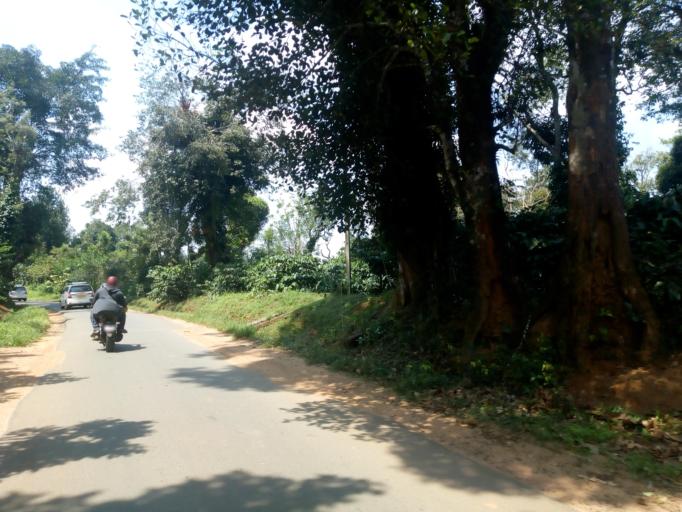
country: IN
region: Karnataka
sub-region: Kodagu
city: Ponnampet
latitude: 12.0308
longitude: 75.9600
